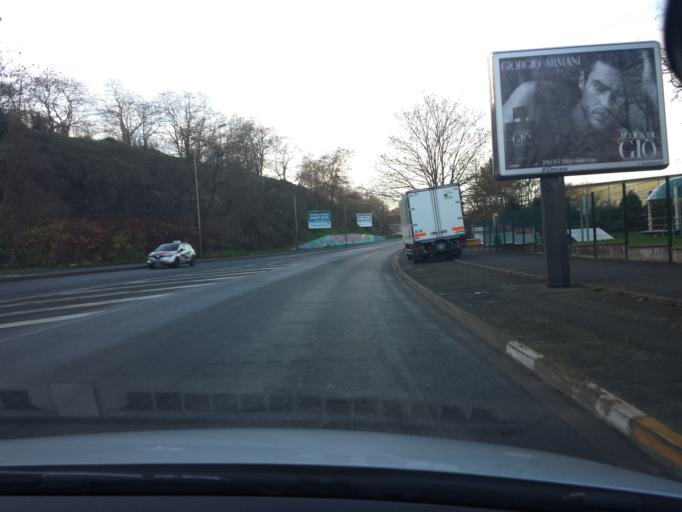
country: FR
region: Ile-de-France
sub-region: Departement de l'Essonne
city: Verrieres-le-Buisson
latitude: 48.7343
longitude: 2.2699
